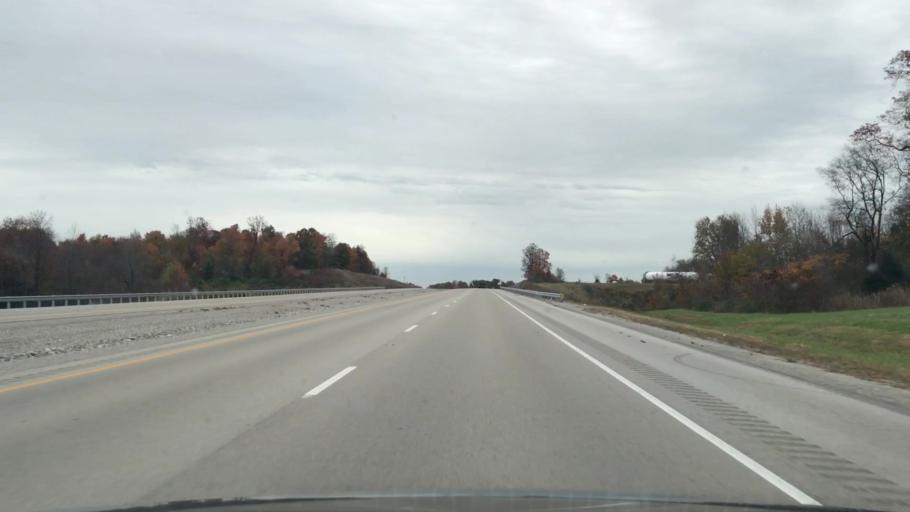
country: US
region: Kentucky
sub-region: Barren County
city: Glasgow
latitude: 37.0063
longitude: -85.9579
